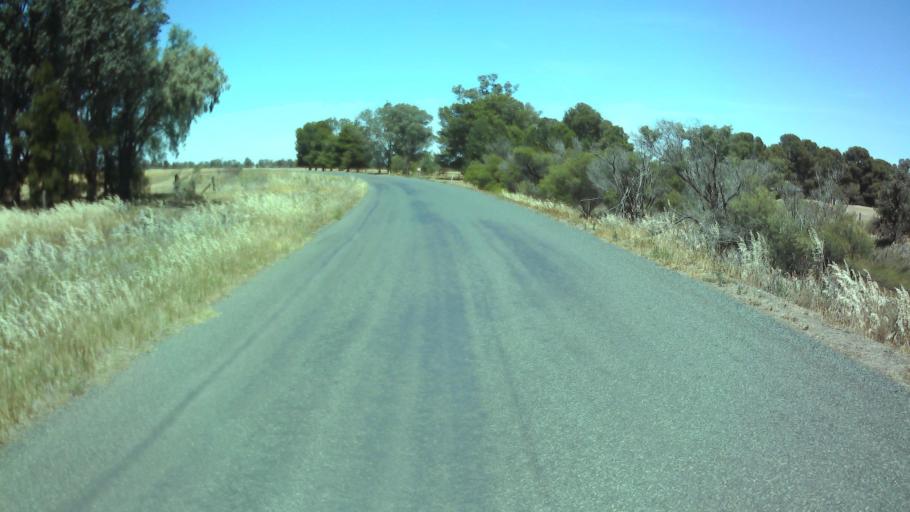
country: AU
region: New South Wales
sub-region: Weddin
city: Grenfell
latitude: -34.0459
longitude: 147.7832
